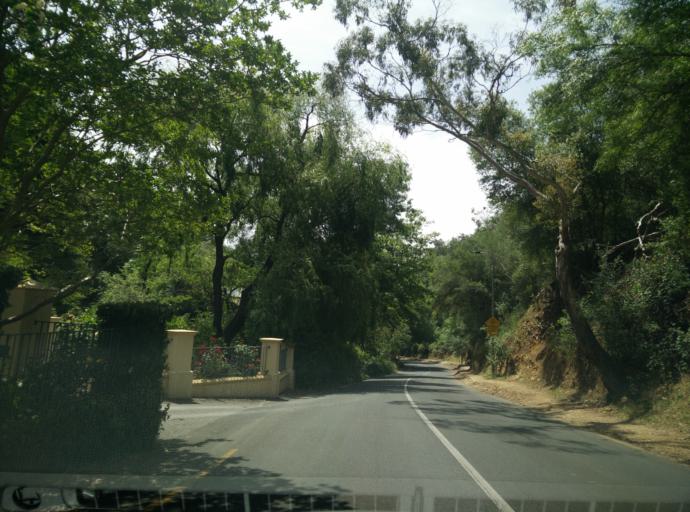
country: AU
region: South Australia
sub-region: Burnside
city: Mount Osmond
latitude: -34.9676
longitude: 138.6798
